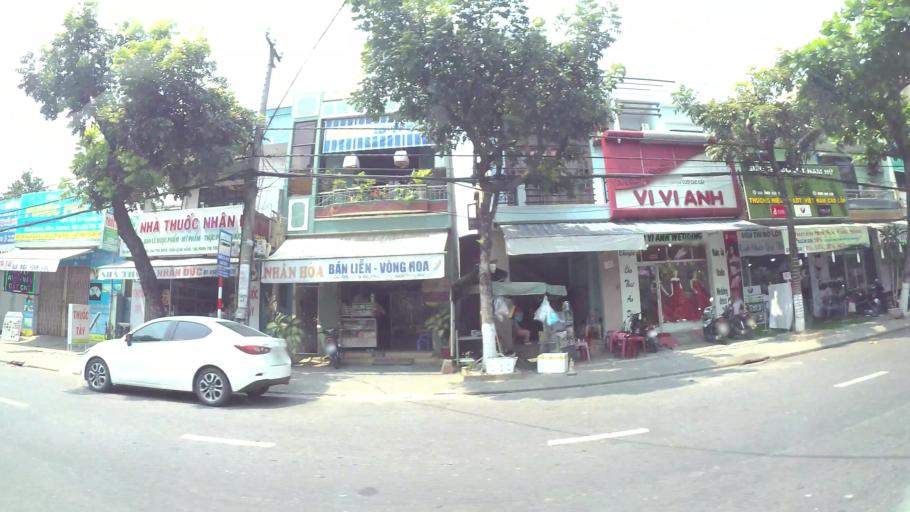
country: VN
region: Da Nang
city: Cam Le
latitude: 16.0125
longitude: 108.2056
